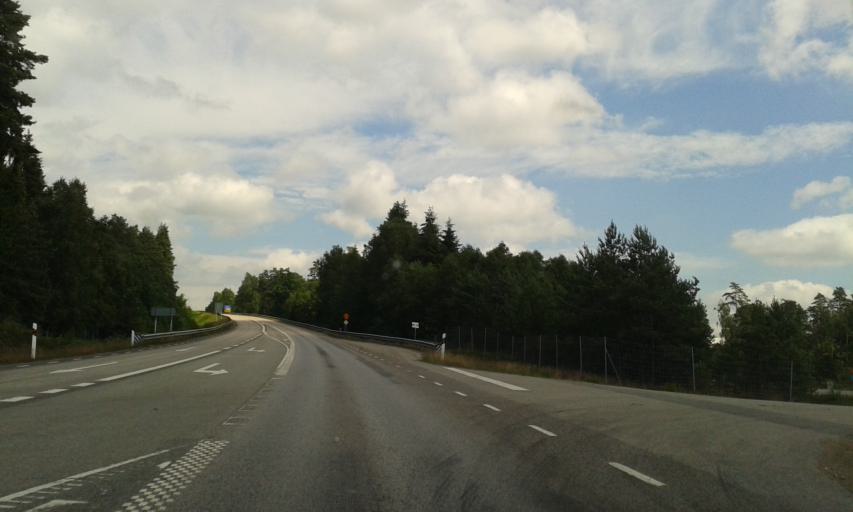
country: SE
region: Kronoberg
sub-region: Alvesta Kommun
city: Alvesta
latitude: 56.9082
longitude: 14.4734
